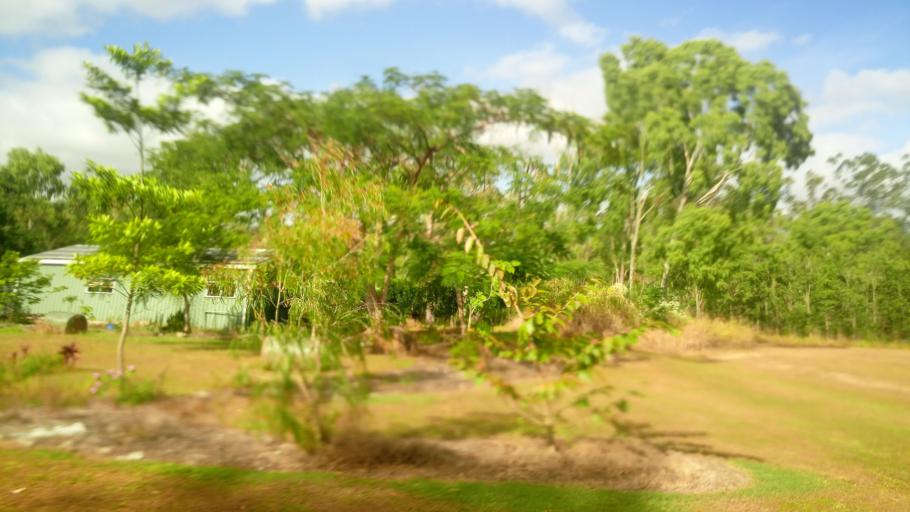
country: AU
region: Queensland
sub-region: Tablelands
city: Mareeba
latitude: -16.9756
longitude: 145.4636
